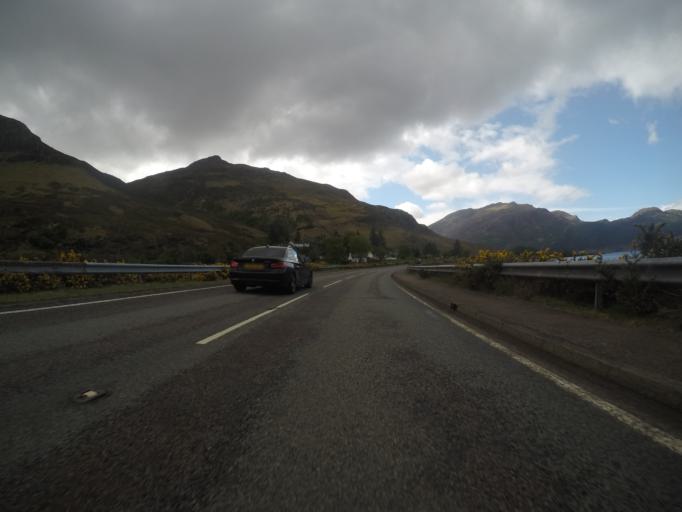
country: GB
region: Scotland
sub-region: Highland
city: Fort William
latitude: 57.2299
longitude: -5.4028
